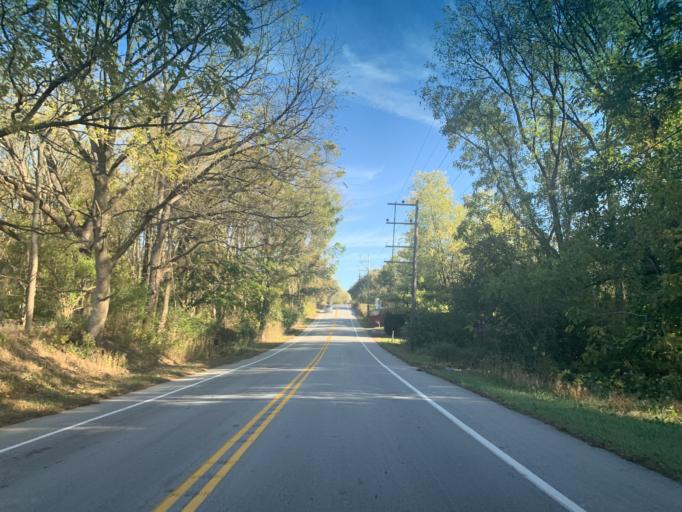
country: US
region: Pennsylvania
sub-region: Chester County
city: Parkesburg
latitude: 39.9289
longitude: -75.9145
